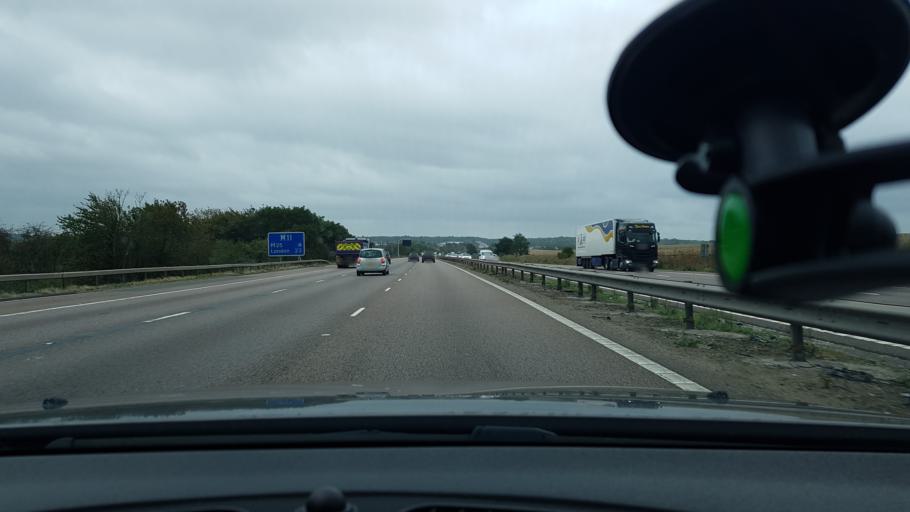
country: GB
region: England
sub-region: Essex
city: Epping
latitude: 51.7355
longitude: 0.1373
